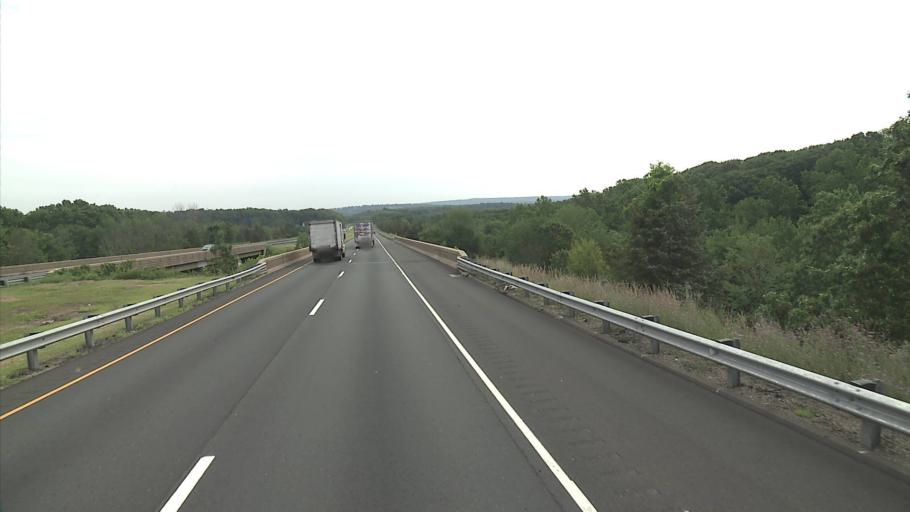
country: US
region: Connecticut
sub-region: New Haven County
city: Middlebury
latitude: 41.5166
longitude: -73.1111
